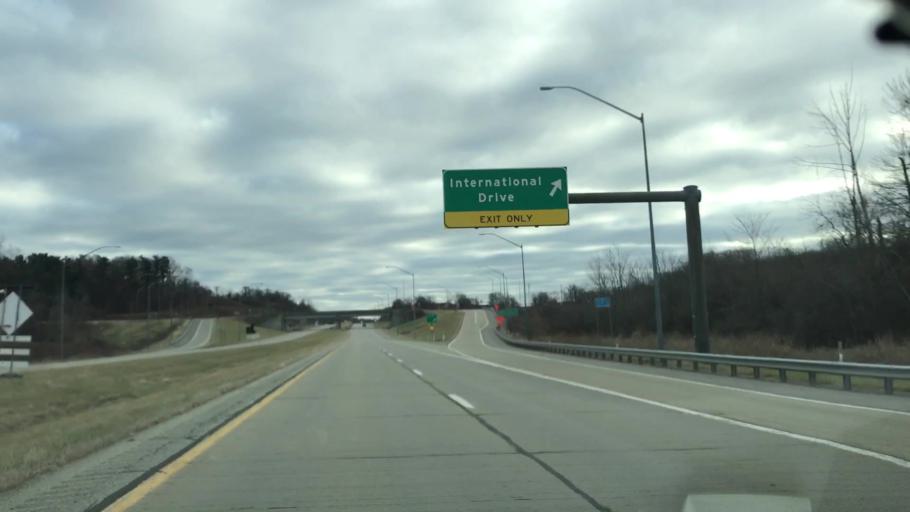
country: US
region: Pennsylvania
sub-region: Allegheny County
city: Carnot-Moon
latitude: 40.5092
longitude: -80.2552
